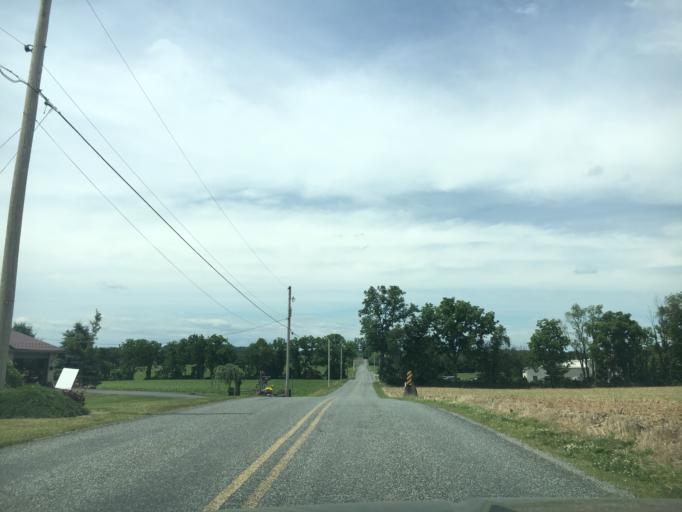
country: US
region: Pennsylvania
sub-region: Berks County
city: Kutztown
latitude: 40.4986
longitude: -75.7887
